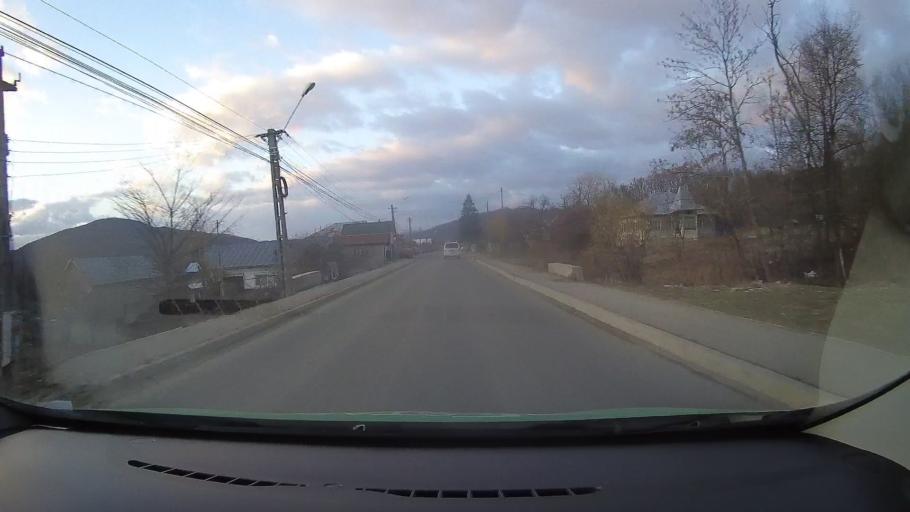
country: RO
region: Dambovita
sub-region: Municipiul Moreni
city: Moreni
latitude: 44.9996
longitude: 25.6474
